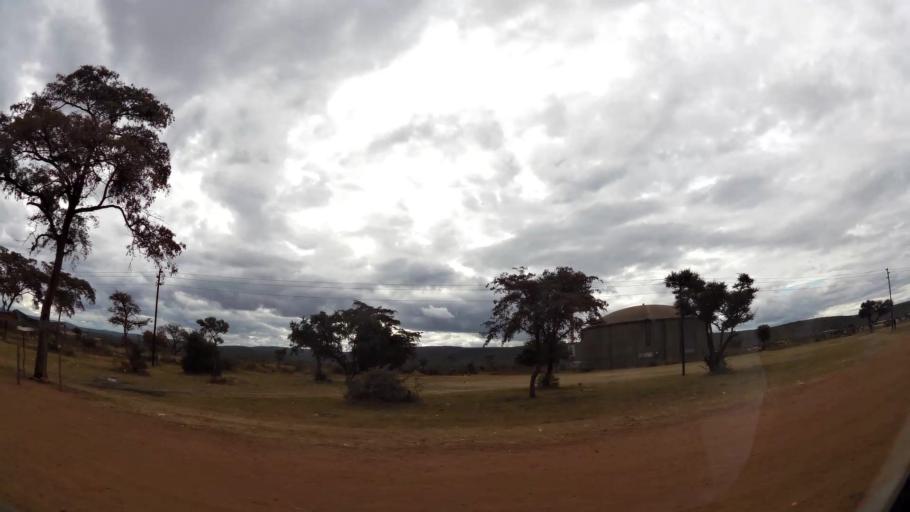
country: ZA
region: Limpopo
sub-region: Waterberg District Municipality
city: Modimolle
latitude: -24.6852
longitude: 28.4250
